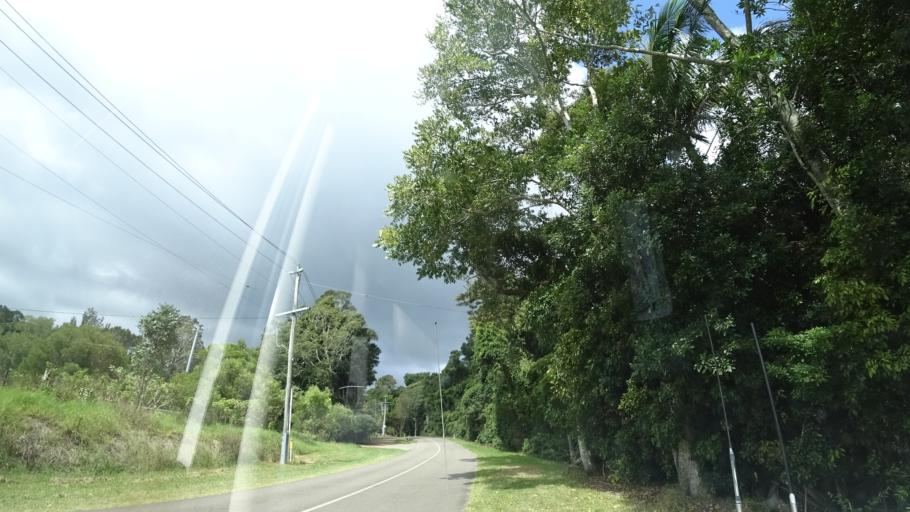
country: AU
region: Queensland
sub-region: Moreton Bay
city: Highvale
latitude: -27.3347
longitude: 152.7658
